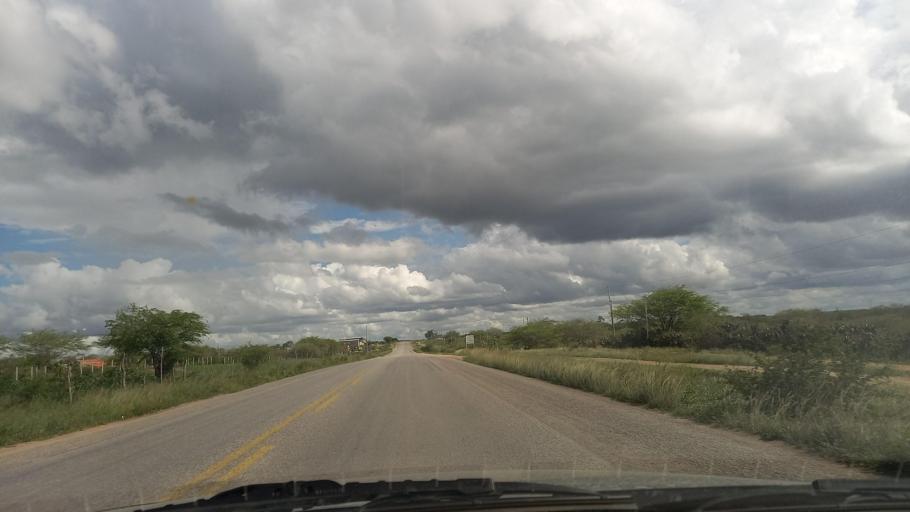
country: BR
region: Pernambuco
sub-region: Cachoeirinha
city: Cachoeirinha
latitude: -8.5041
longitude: -36.2480
